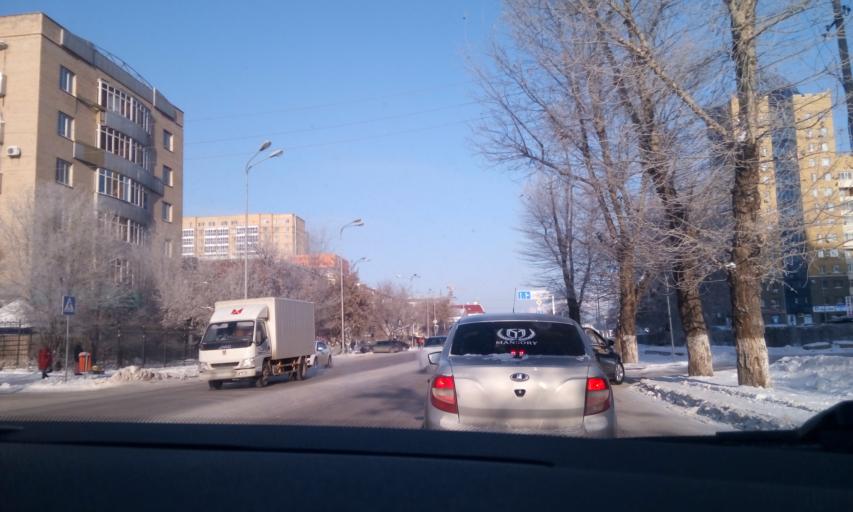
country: KZ
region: Astana Qalasy
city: Astana
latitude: 51.1686
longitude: 71.4395
